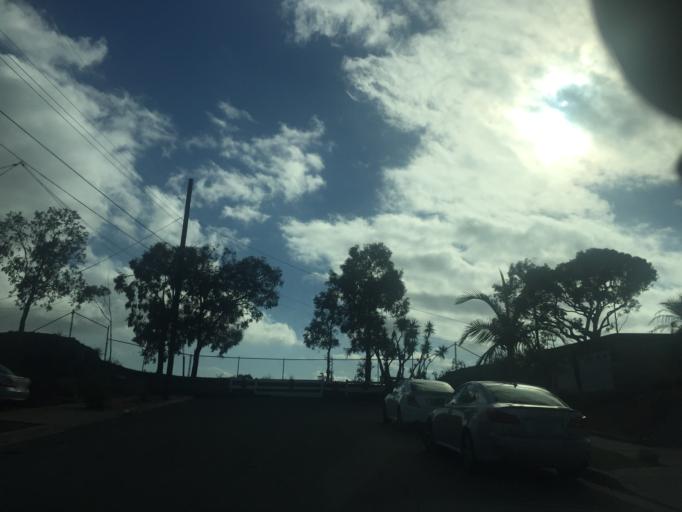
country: US
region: California
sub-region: San Diego County
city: San Diego
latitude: 32.7806
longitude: -117.1515
